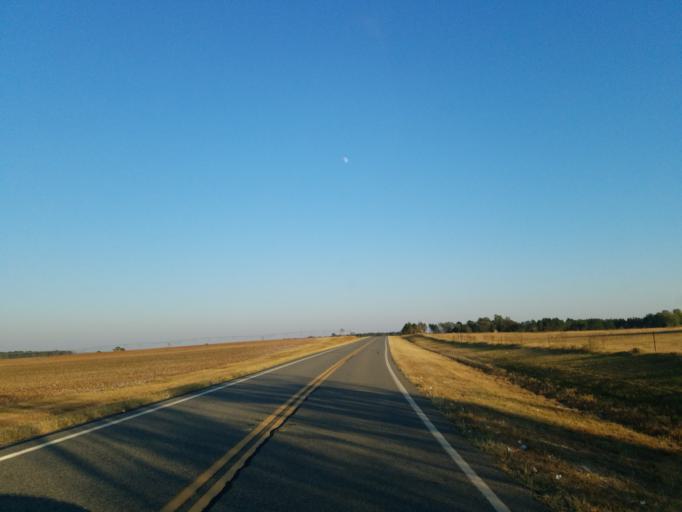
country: US
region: Georgia
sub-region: Turner County
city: Ashburn
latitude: 31.8597
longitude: -83.5987
